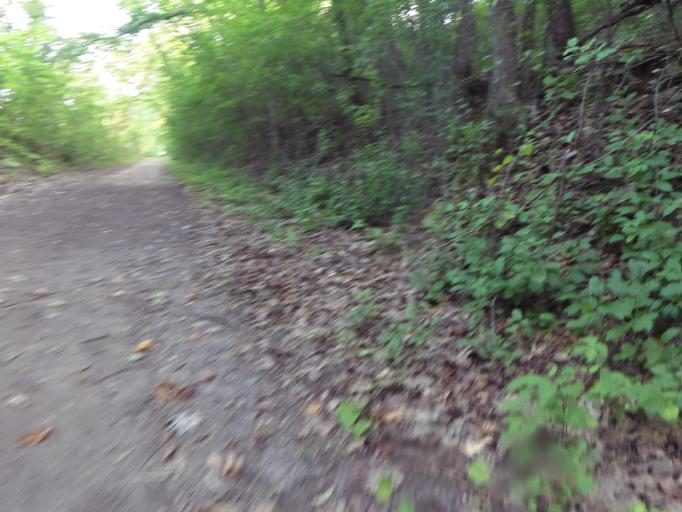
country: US
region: Minnesota
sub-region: Washington County
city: Afton
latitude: 44.8515
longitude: -92.7722
